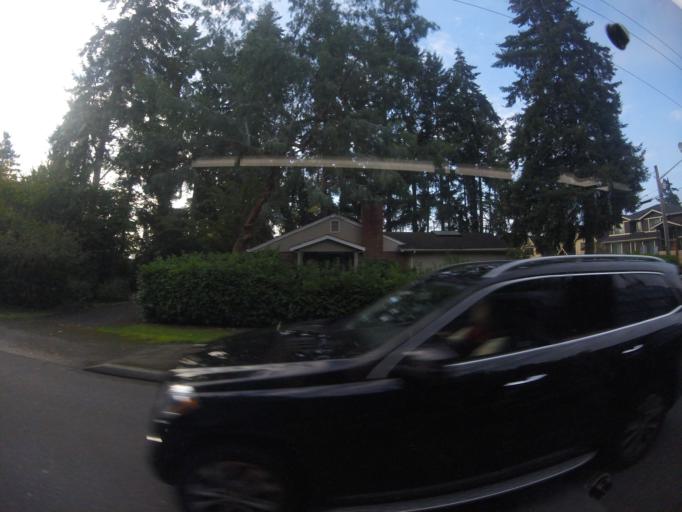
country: US
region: Washington
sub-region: King County
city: Bellevue
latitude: 47.6175
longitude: -122.2116
